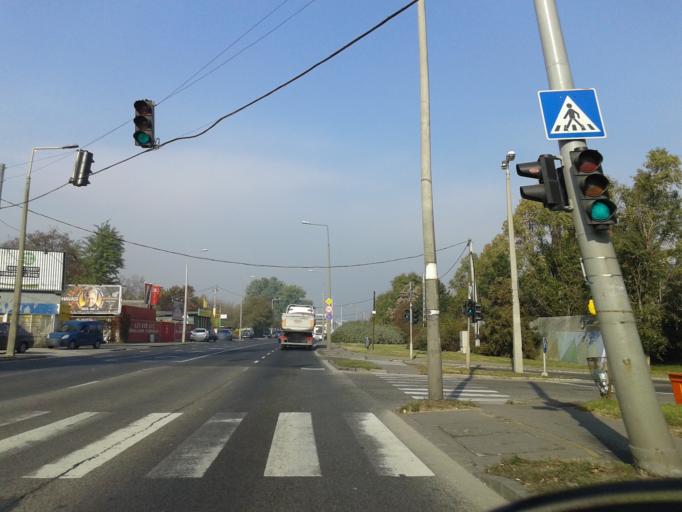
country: HU
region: Budapest
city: Budapest III. keruelet
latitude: 47.5568
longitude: 19.0263
